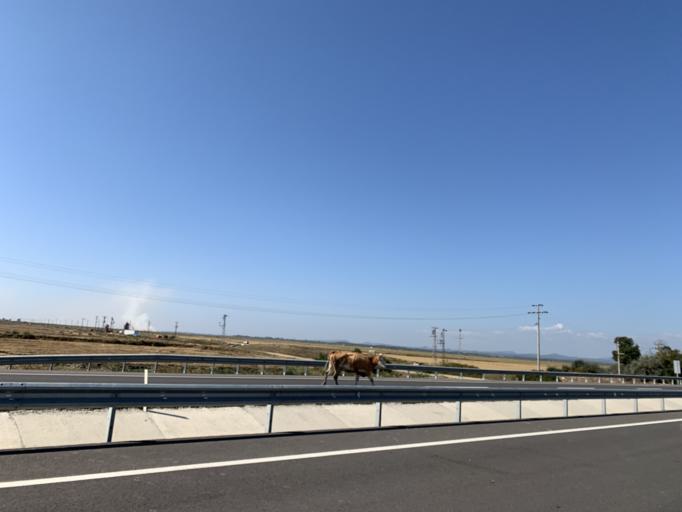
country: TR
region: Edirne
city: Ipsala
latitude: 40.9149
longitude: 26.3602
